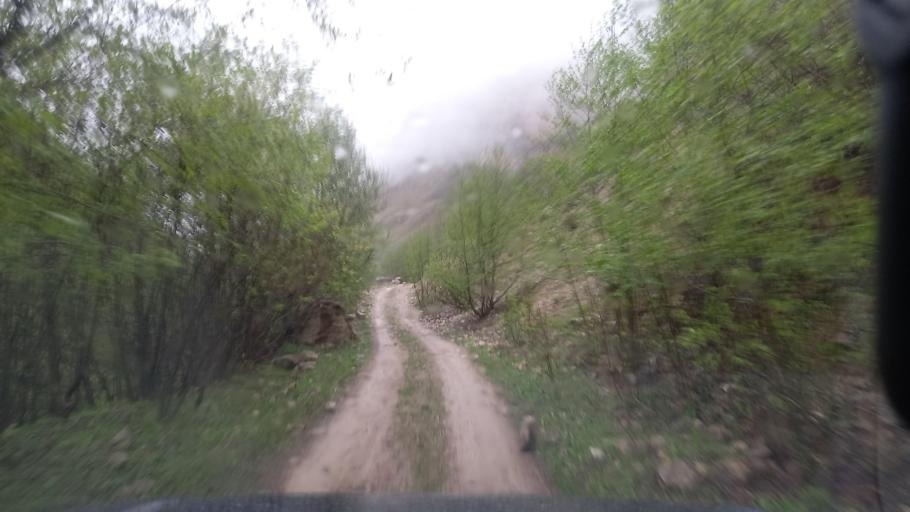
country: RU
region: Kabardino-Balkariya
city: Bylym
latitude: 43.5990
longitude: 42.9453
